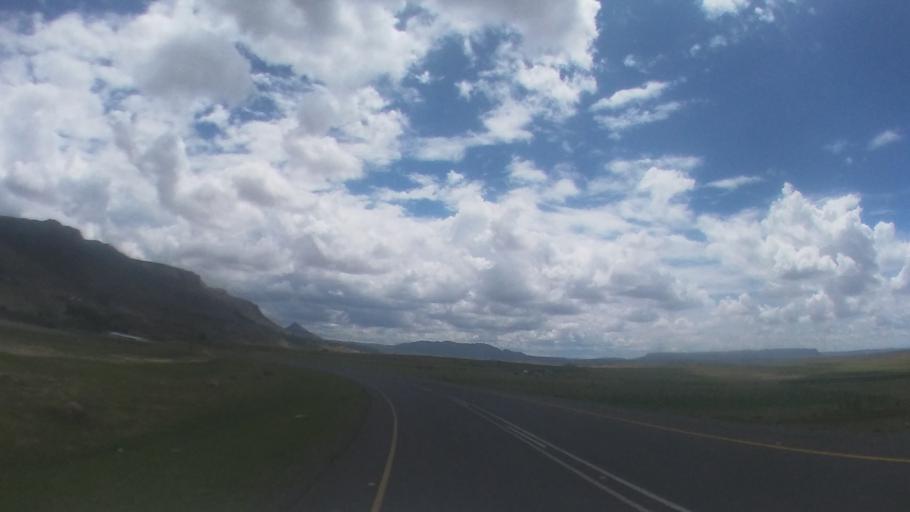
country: LS
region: Maseru
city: Maseru
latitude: -29.4483
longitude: 27.4782
